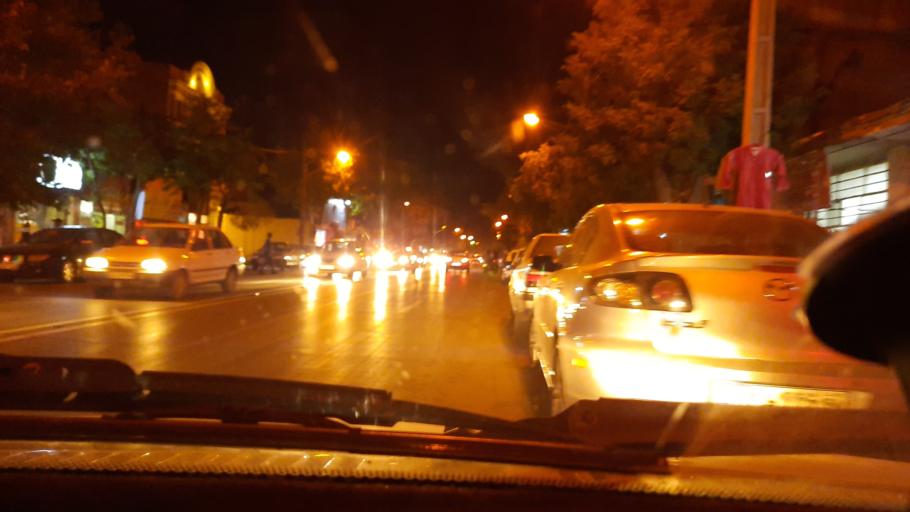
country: IR
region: Markazi
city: Arak
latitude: 34.0920
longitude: 49.7001
